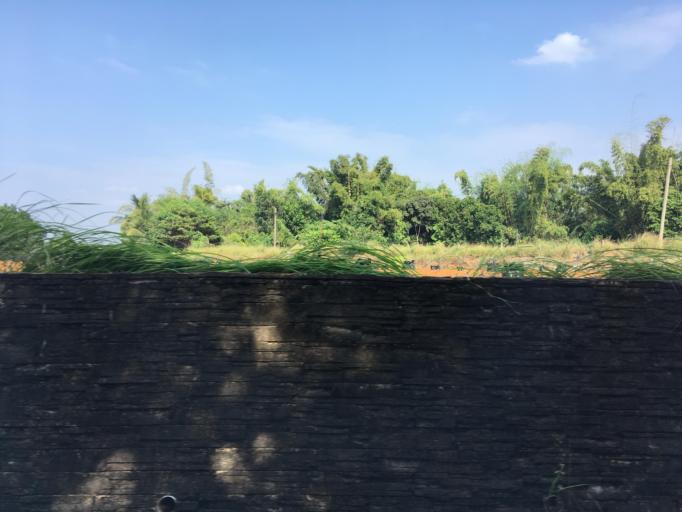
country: TW
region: Taiwan
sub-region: Chiayi
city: Jiayi Shi
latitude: 23.4970
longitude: 120.4828
